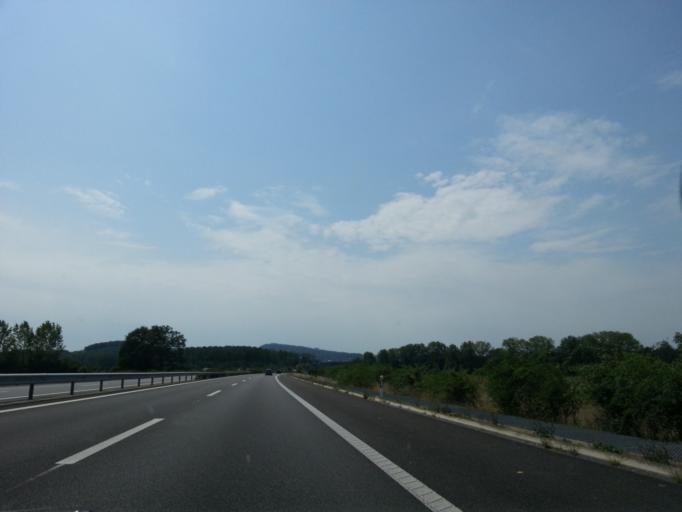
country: CH
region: Vaud
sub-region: Broye-Vully District
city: Payerne
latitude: 46.8326
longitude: 6.9166
